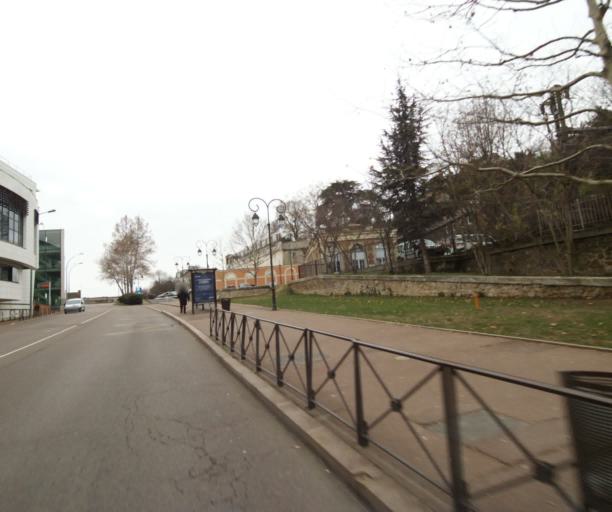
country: FR
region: Ile-de-France
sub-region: Departement des Hauts-de-Seine
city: Saint-Cloud
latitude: 48.8448
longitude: 2.2174
